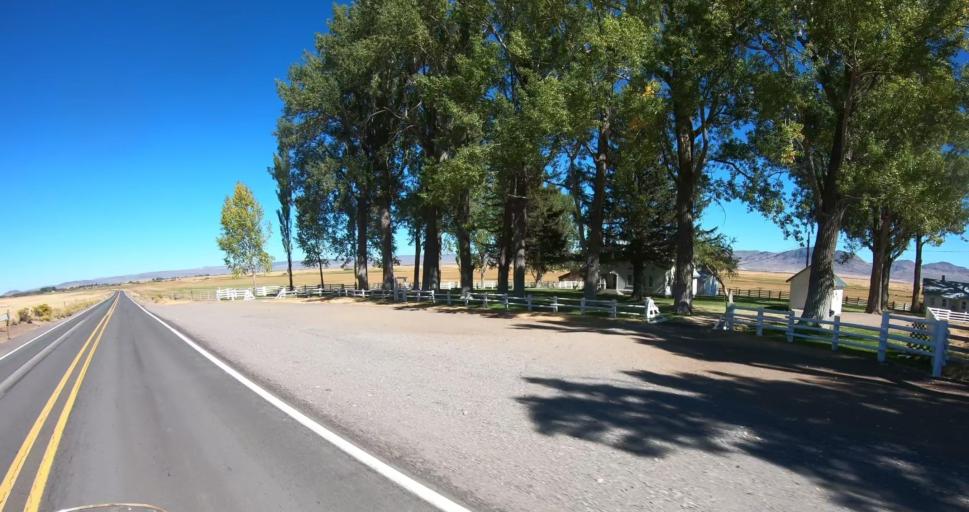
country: US
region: Oregon
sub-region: Lake County
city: Lakeview
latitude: 42.6607
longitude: -120.5235
